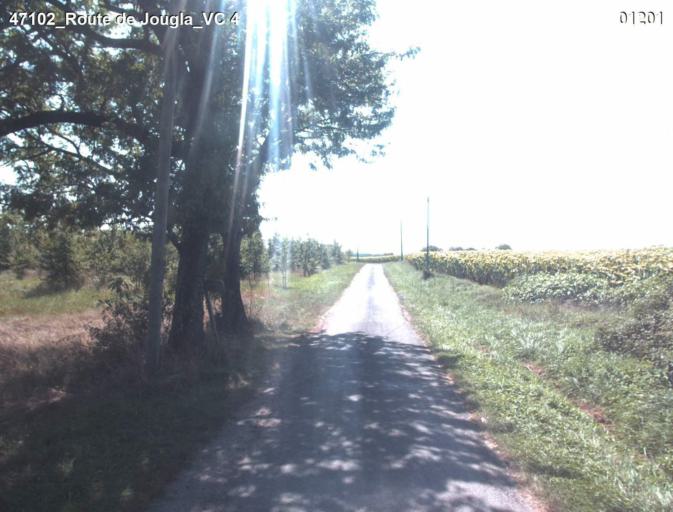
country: FR
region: Aquitaine
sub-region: Departement du Lot-et-Garonne
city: Laplume
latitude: 44.0539
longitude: 0.4394
